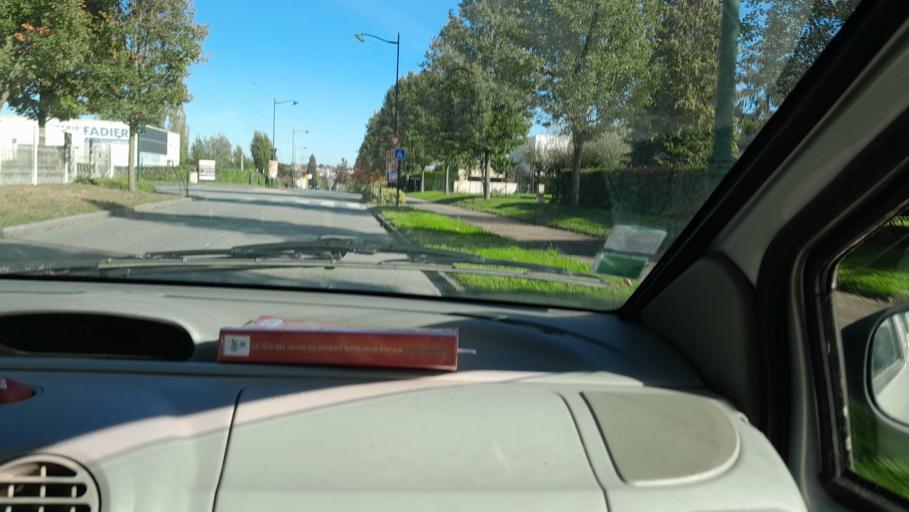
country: FR
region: Brittany
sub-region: Departement d'Ille-et-Vilaine
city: Argentre-du-Plessis
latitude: 48.0565
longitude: -1.1671
